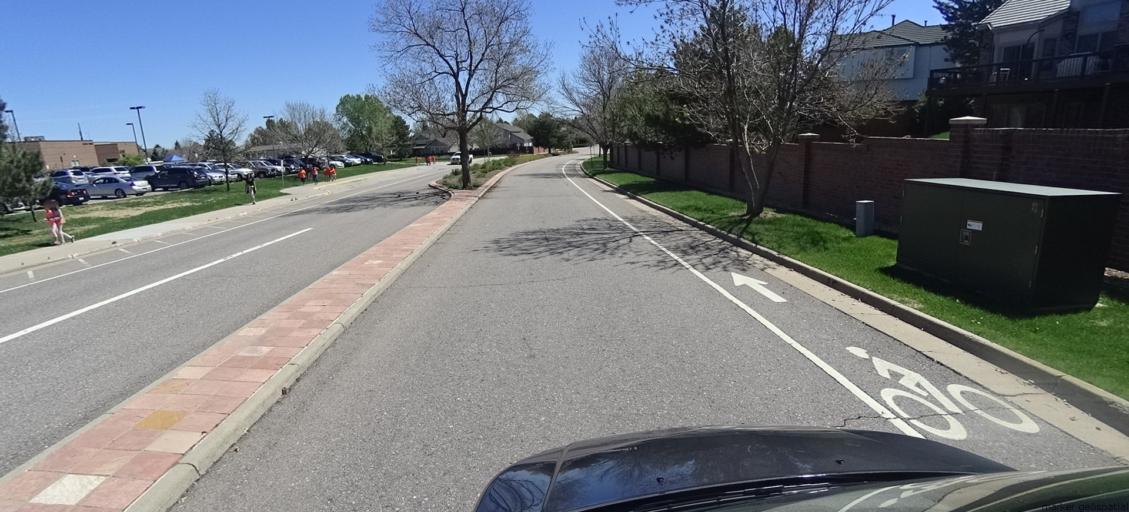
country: US
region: Colorado
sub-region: Douglas County
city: Acres Green
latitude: 39.5460
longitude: -104.9009
